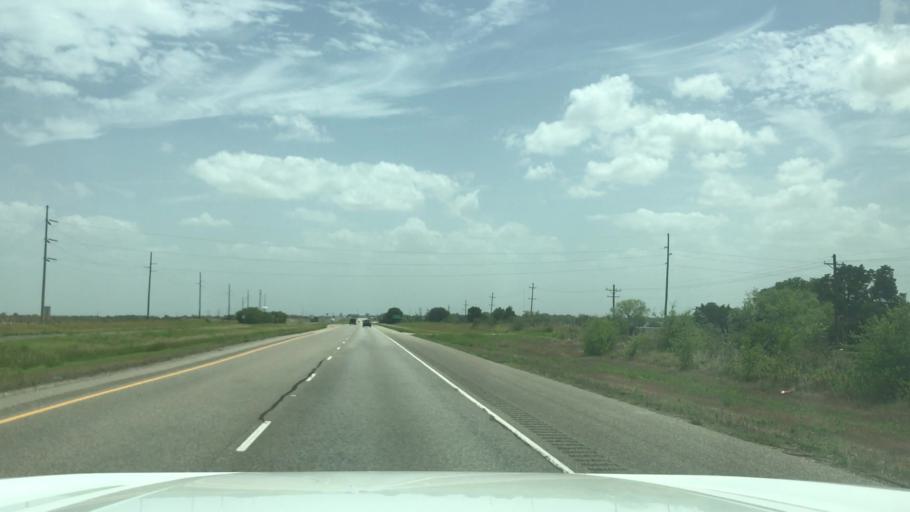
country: US
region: Texas
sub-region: Falls County
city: Marlin
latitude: 31.3400
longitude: -96.8927
